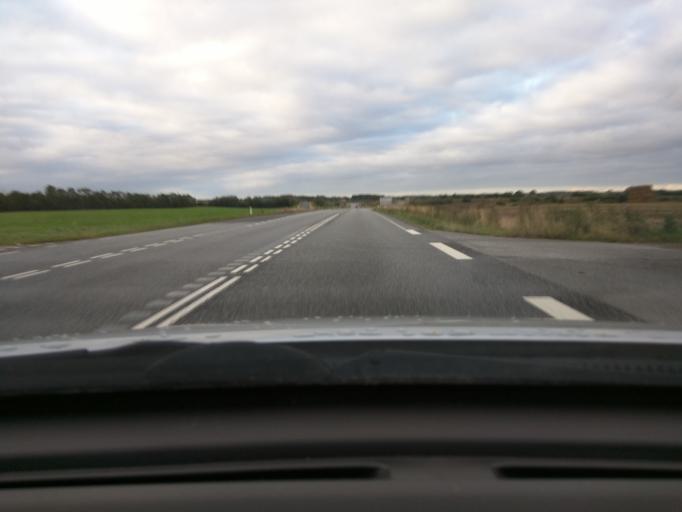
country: DK
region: Central Jutland
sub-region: Silkeborg Kommune
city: Kjellerup
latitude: 56.3043
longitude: 9.3244
